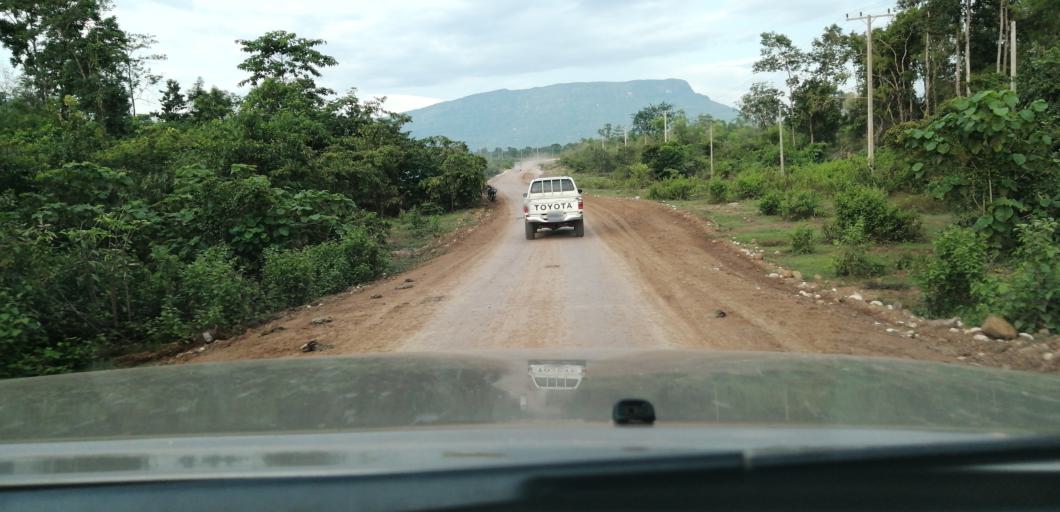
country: LA
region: Attapu
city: Attapu
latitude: 14.7093
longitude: 106.4819
